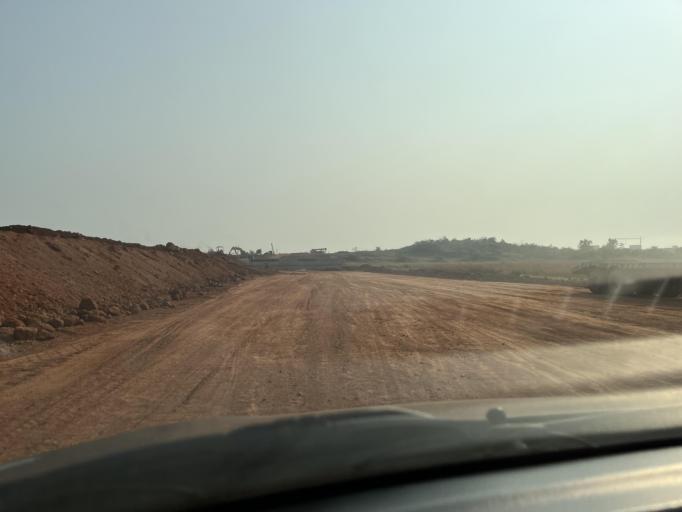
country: IN
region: Goa
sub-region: North Goa
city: Pernem
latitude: 15.6917
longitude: 73.8383
